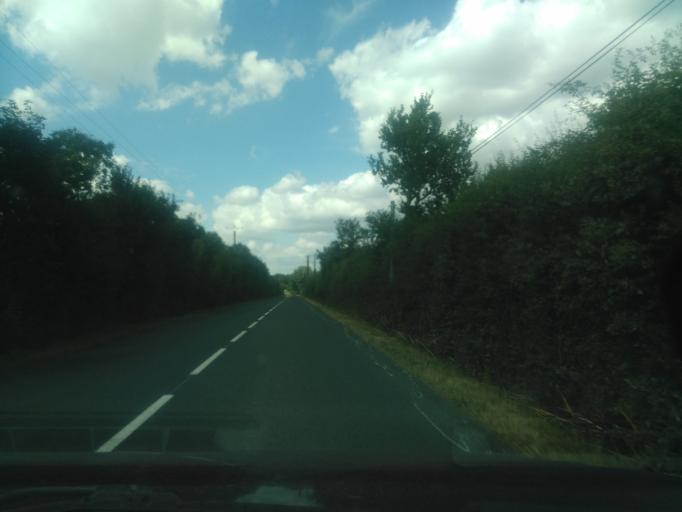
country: FR
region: Pays de la Loire
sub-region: Departement de la Vendee
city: Chauche
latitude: 46.8463
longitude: -1.2936
